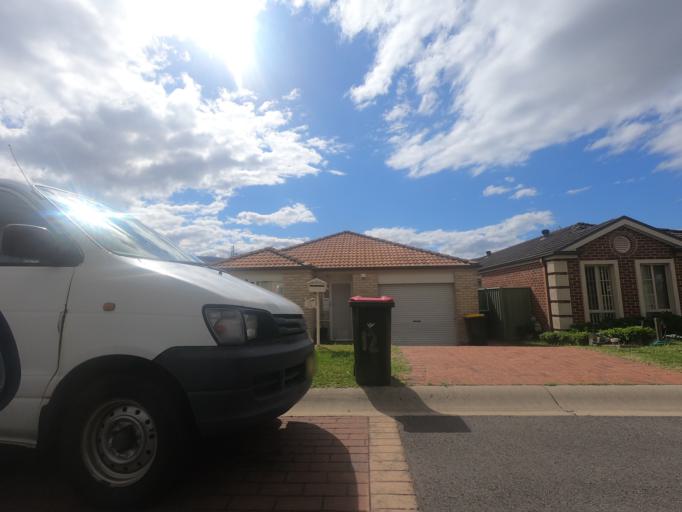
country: AU
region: New South Wales
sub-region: Wollongong
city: Dapto
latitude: -34.4863
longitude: 150.7764
